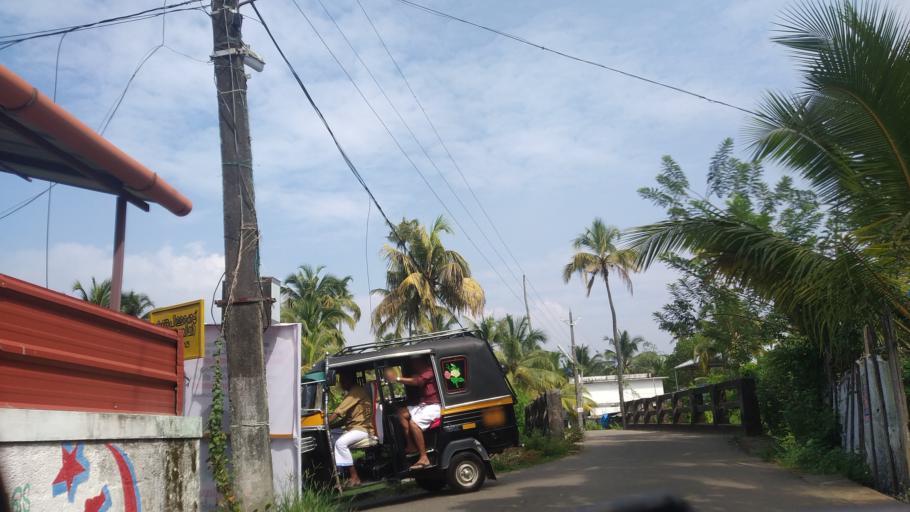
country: IN
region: Kerala
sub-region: Ernakulam
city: Elur
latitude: 10.0879
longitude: 76.2014
